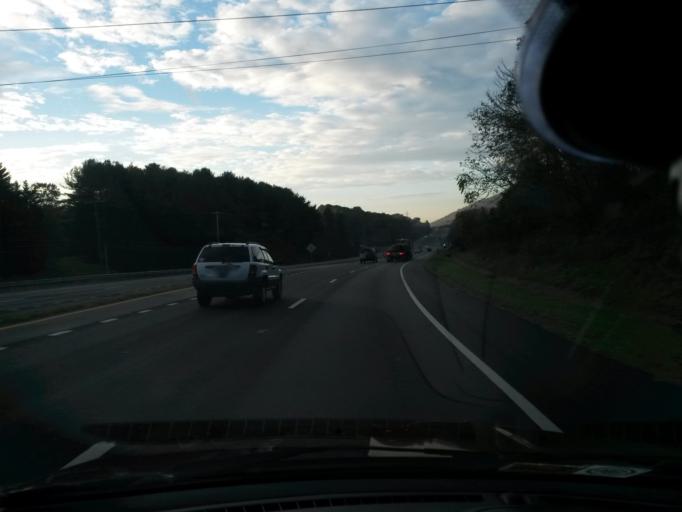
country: US
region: Virginia
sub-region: Botetourt County
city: Cloverdale
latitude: 37.3747
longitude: -79.8866
